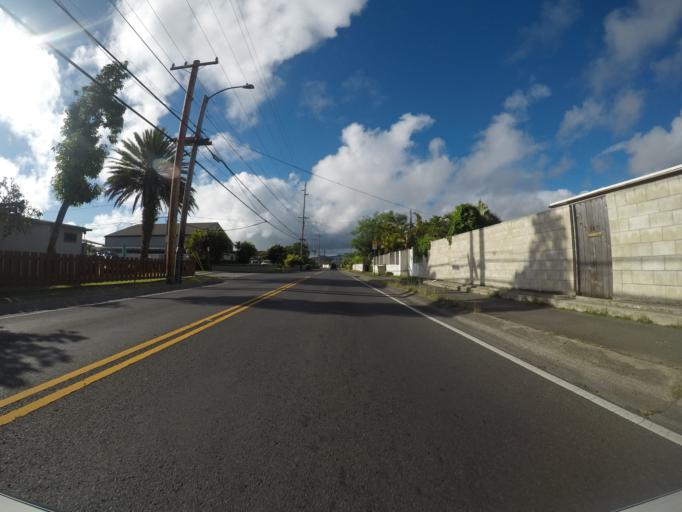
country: US
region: Hawaii
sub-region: Honolulu County
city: Kailua
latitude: 21.3986
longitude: -157.7471
